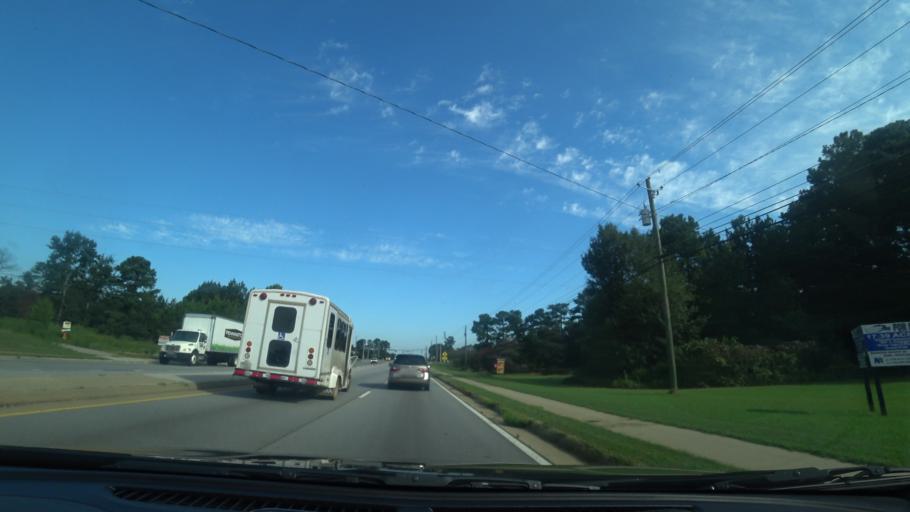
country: US
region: Georgia
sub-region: Gwinnett County
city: Grayson
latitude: 33.9102
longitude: -83.9685
